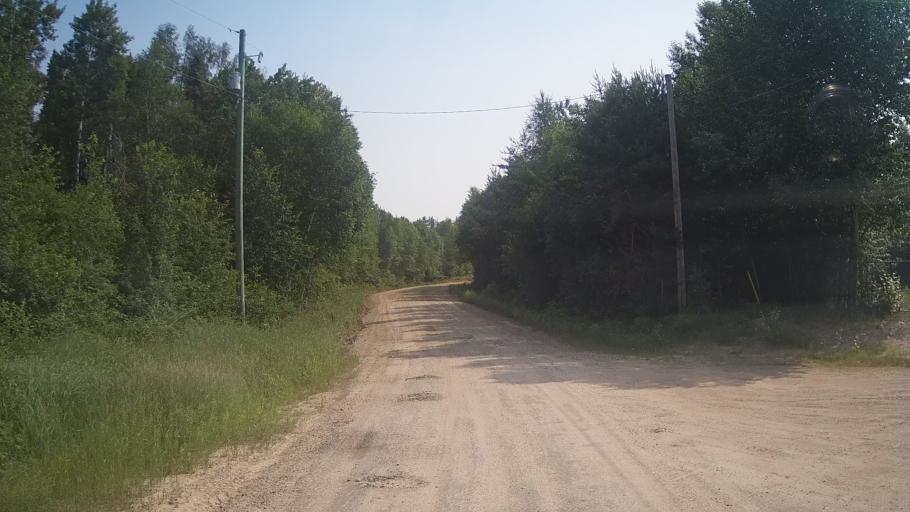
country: CA
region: Ontario
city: Timmins
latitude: 47.6770
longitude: -81.7215
